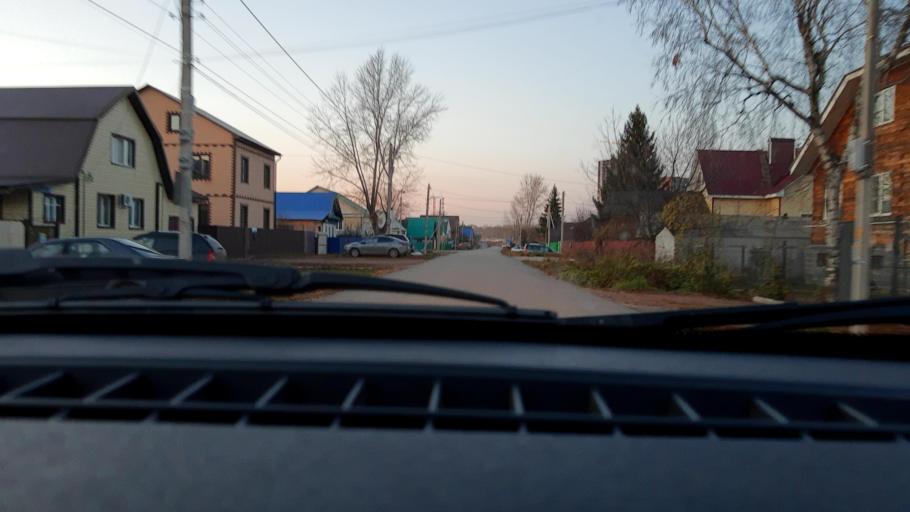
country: RU
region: Bashkortostan
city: Mikhaylovka
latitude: 54.7647
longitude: 55.9020
